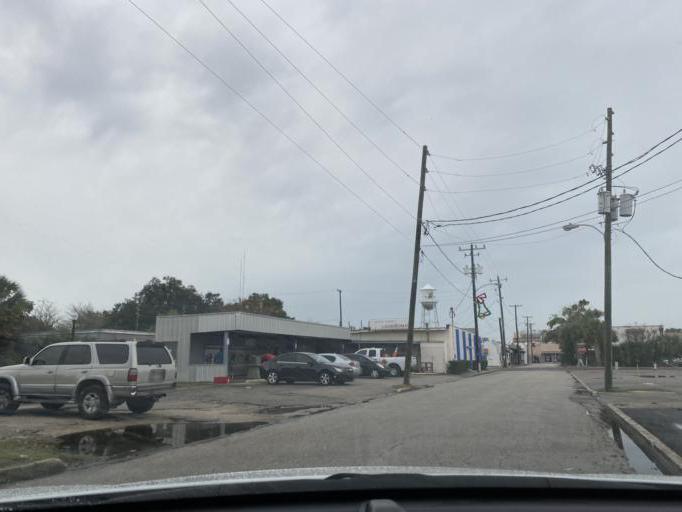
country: US
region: Florida
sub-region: Orange County
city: Winter Garden
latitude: 28.5651
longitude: -81.5838
